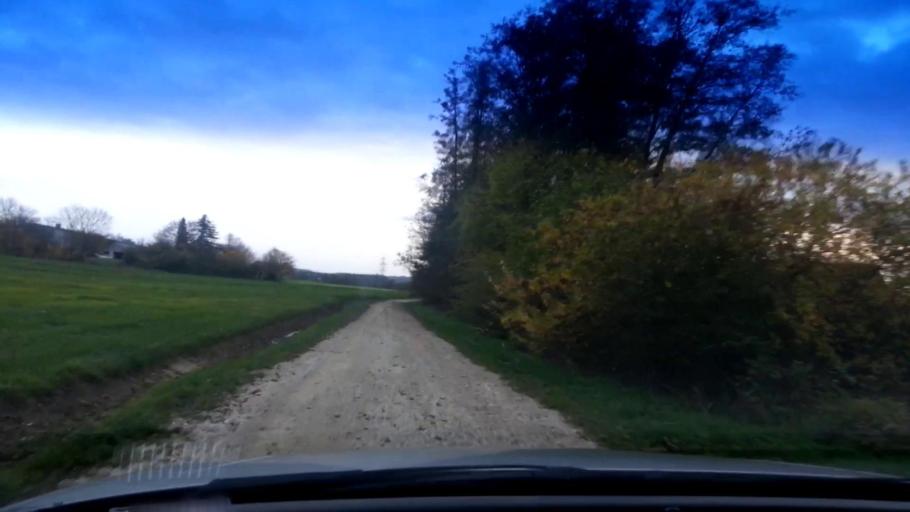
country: DE
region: Bavaria
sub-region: Upper Franconia
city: Memmelsdorf
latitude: 49.9612
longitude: 10.9621
